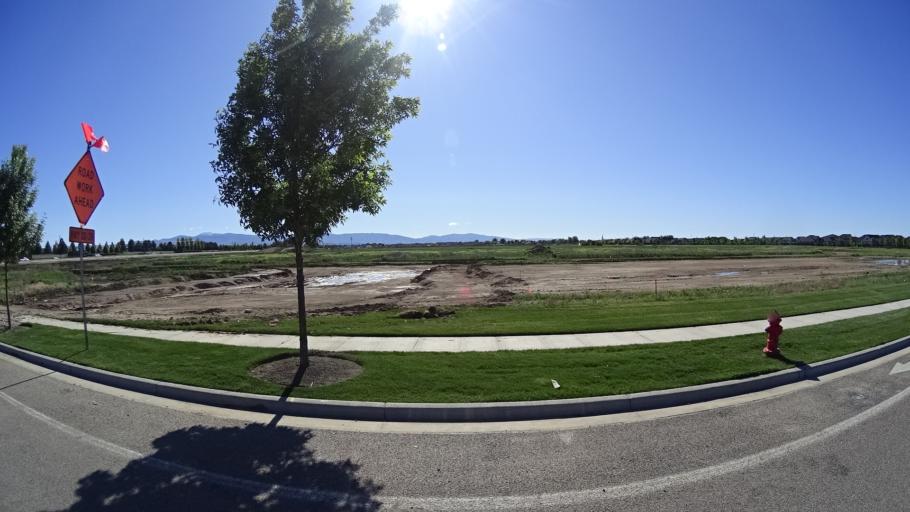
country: US
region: Idaho
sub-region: Ada County
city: Star
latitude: 43.6617
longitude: -116.4436
